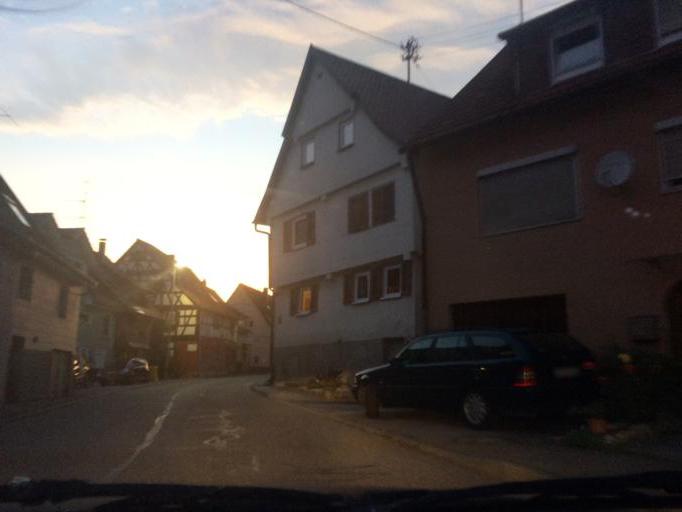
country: DE
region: Baden-Wuerttemberg
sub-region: Regierungsbezirk Stuttgart
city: Schorndorf
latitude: 48.8318
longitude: 9.5109
